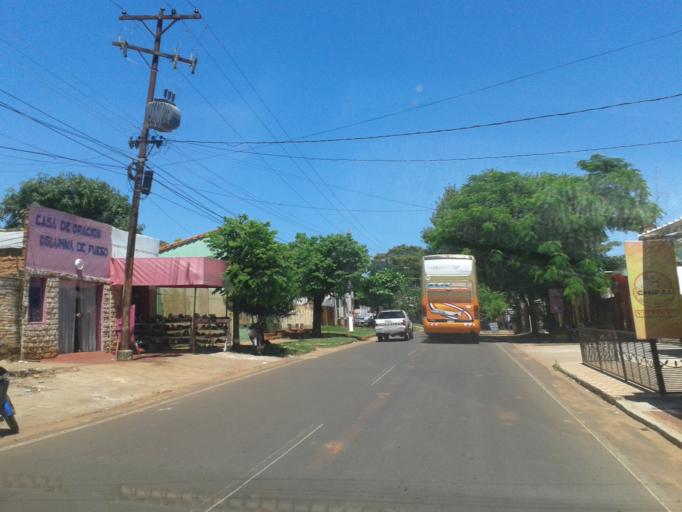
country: PY
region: Misiones
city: Santa Maria
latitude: -26.8864
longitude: -57.0204
